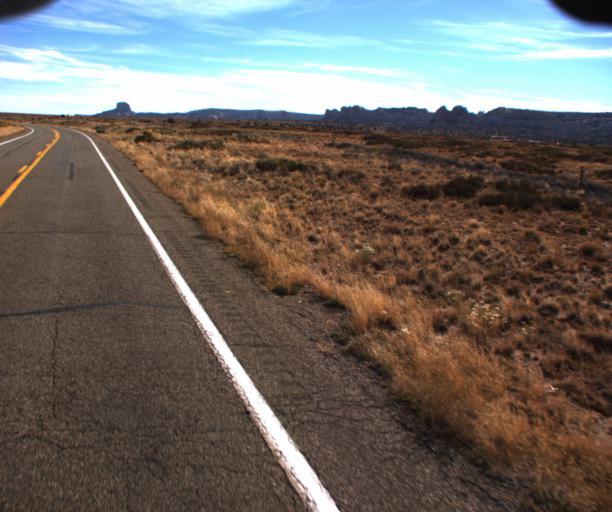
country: US
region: Arizona
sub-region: Coconino County
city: Kaibito
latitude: 36.6120
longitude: -111.0172
